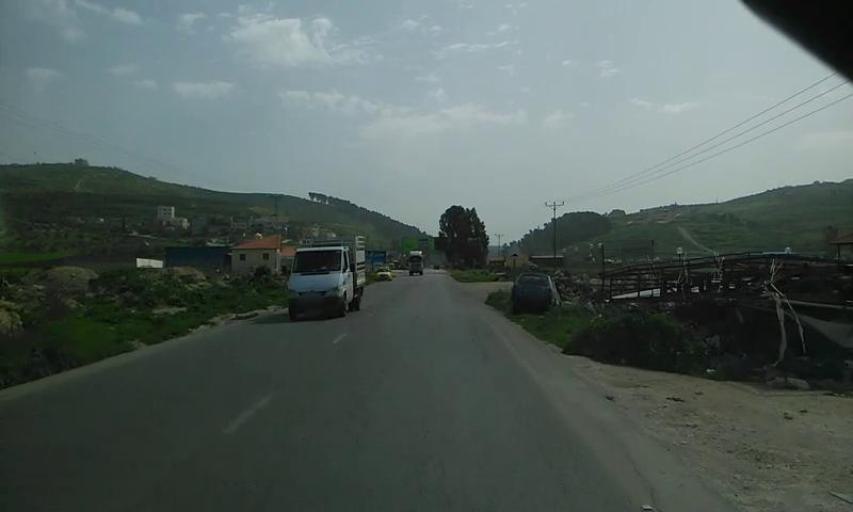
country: PS
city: Bir al Basha
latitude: 32.4108
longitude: 35.2278
